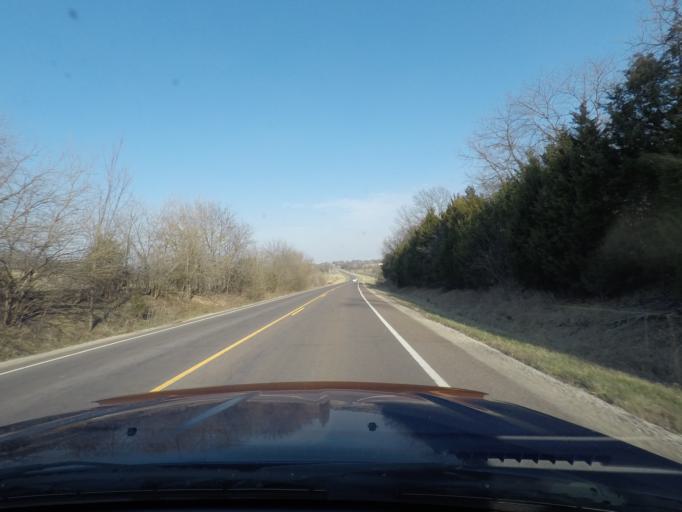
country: US
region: Kansas
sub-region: Douglas County
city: Lawrence
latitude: 39.0009
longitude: -95.3054
